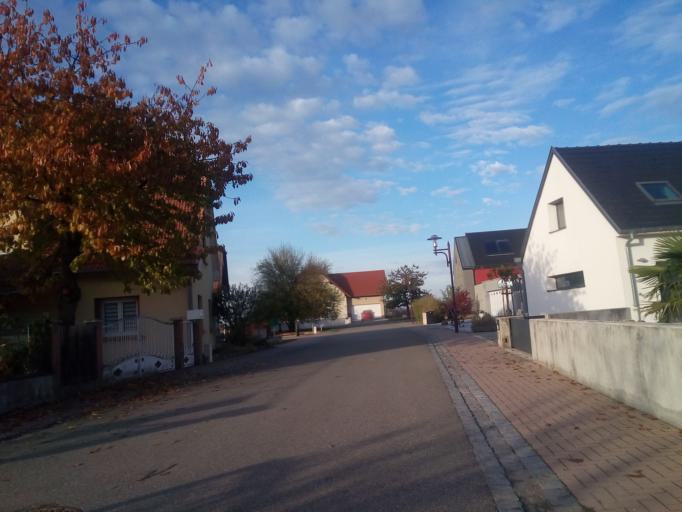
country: FR
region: Alsace
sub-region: Departement du Bas-Rhin
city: Herrlisheim
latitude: 48.7162
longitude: 7.9186
